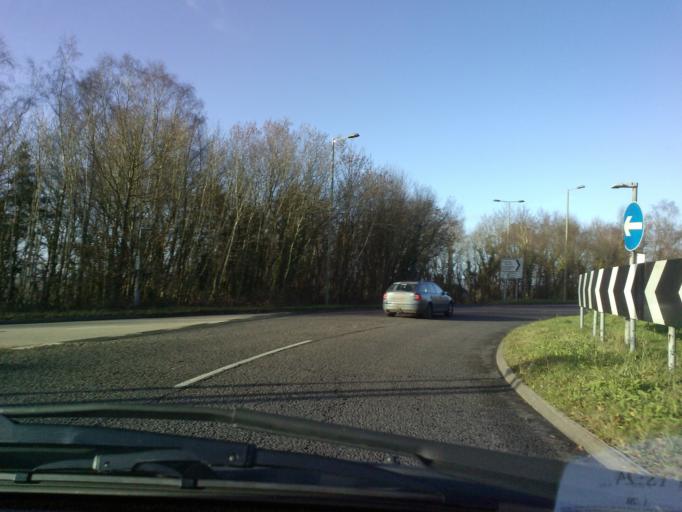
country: GB
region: England
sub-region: Hampshire
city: Totton
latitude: 50.9550
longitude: -1.4730
